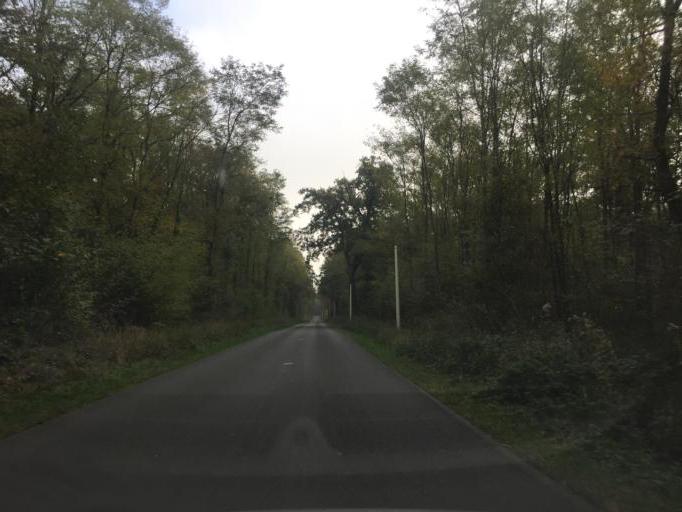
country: FR
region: Rhone-Alpes
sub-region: Departement de l'Ain
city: Tramoyes
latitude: 45.9007
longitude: 4.9651
